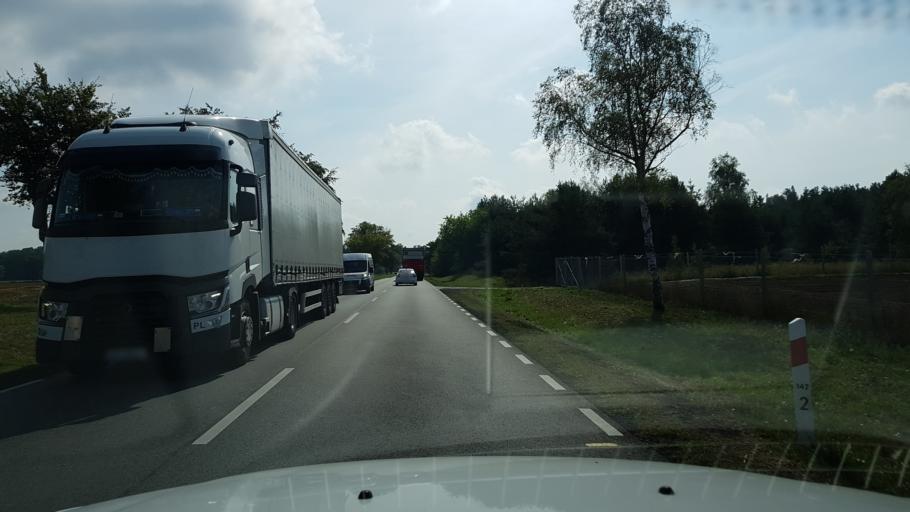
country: PL
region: West Pomeranian Voivodeship
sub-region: Powiat walecki
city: Walcz
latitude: 53.3173
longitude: 16.3324
